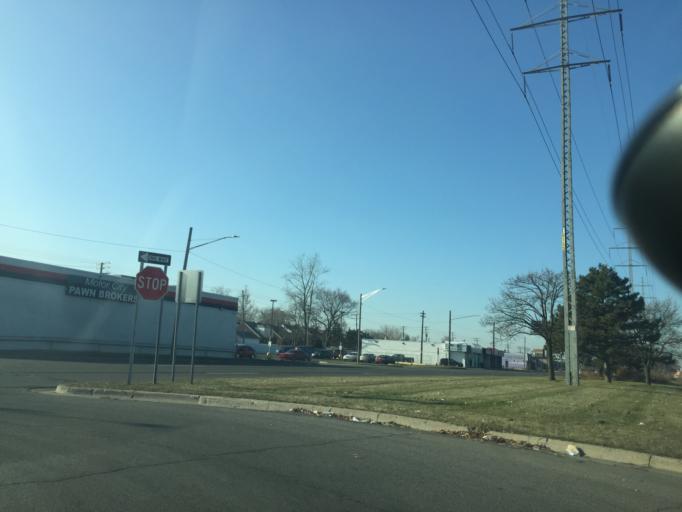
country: US
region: Michigan
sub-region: Macomb County
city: Eastpointe
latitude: 42.4501
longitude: -82.9623
